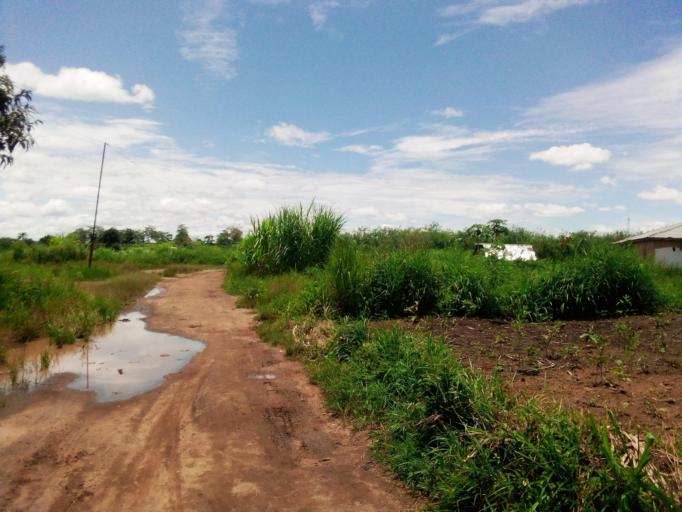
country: SL
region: Eastern Province
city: Koidu
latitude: 8.6431
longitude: -10.9259
